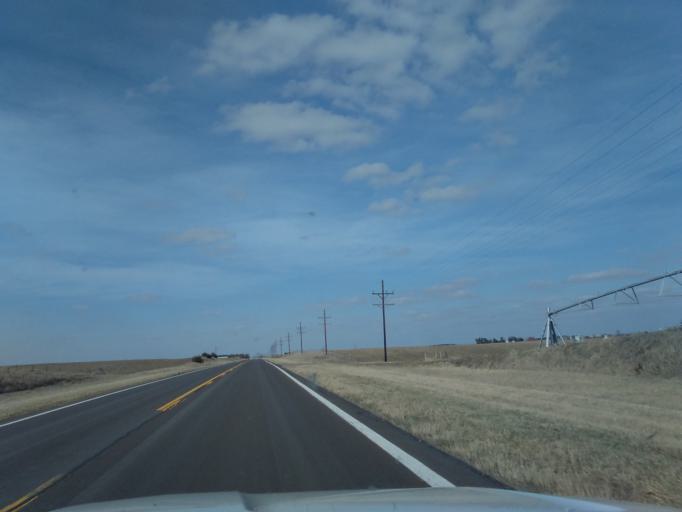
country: US
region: Nebraska
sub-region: Gage County
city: Beatrice
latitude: 40.1565
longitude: -96.9352
